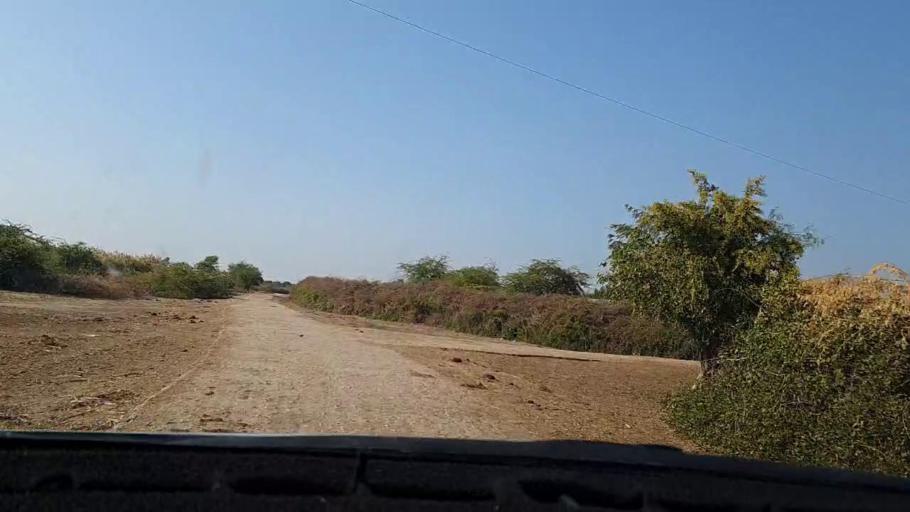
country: PK
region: Sindh
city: Tando Mittha Khan
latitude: 25.8111
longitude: 69.3280
